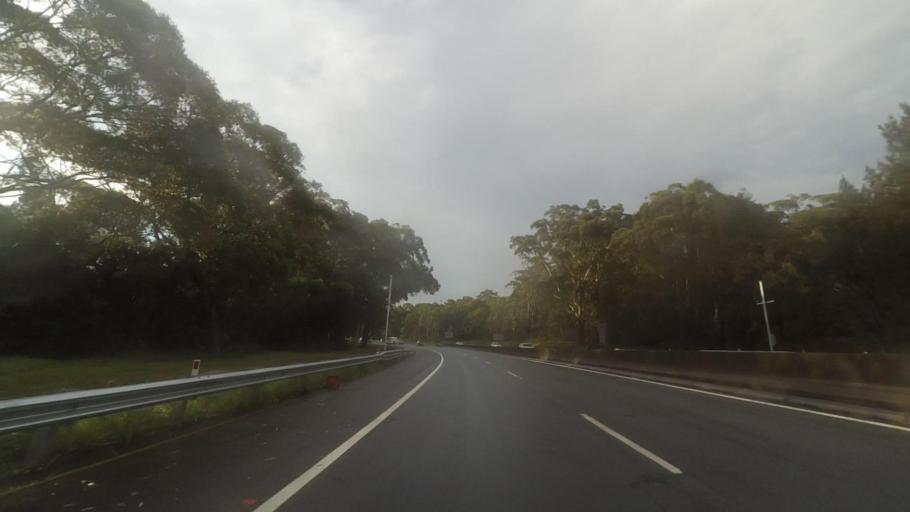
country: AU
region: New South Wales
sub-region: Wollongong
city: Mount Ousley
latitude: -34.4039
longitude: 150.8833
